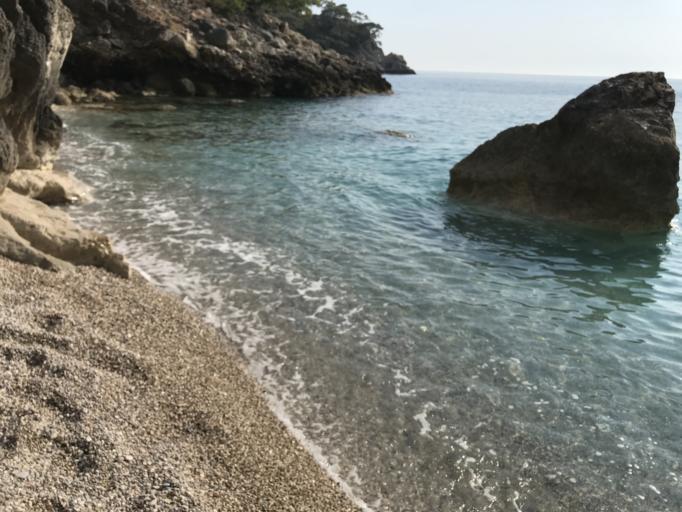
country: TR
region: Mugla
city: OEluedeniz
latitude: 36.4396
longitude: 29.1316
